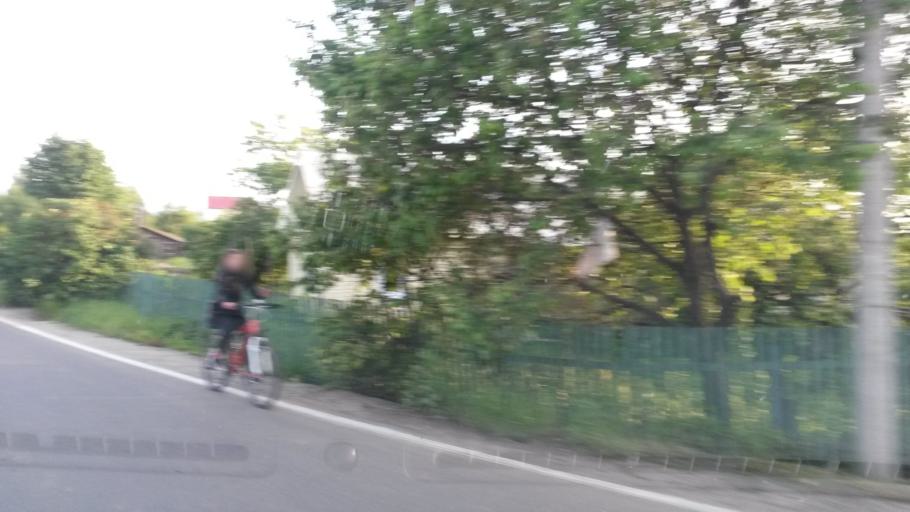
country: RU
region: Jaroslavl
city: Yaroslavl
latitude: 57.7114
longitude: 39.8357
